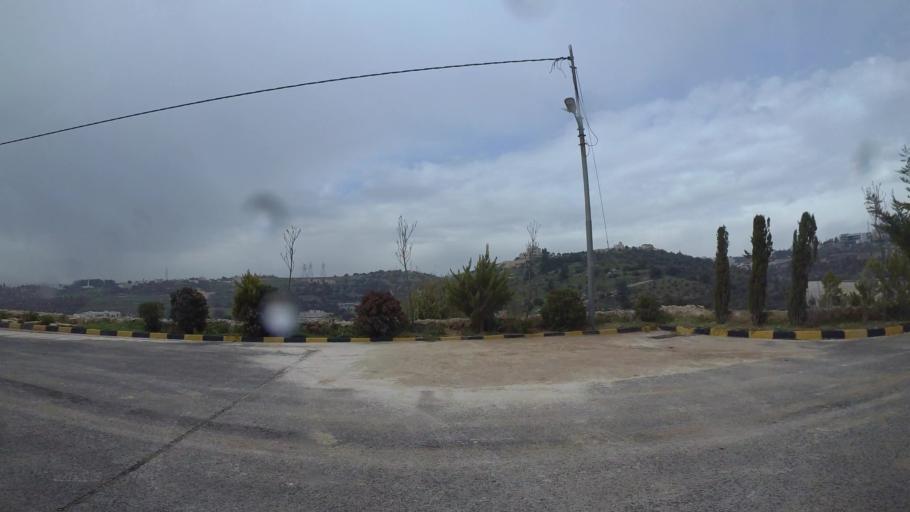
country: JO
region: Amman
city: Wadi as Sir
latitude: 31.9872
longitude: 35.8165
